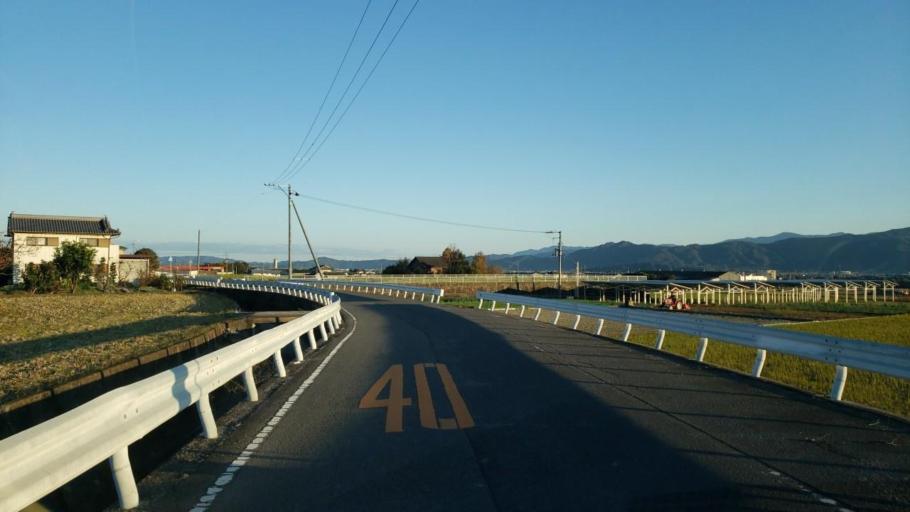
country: JP
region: Tokushima
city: Kamojimacho-jogejima
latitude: 34.1132
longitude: 134.3465
